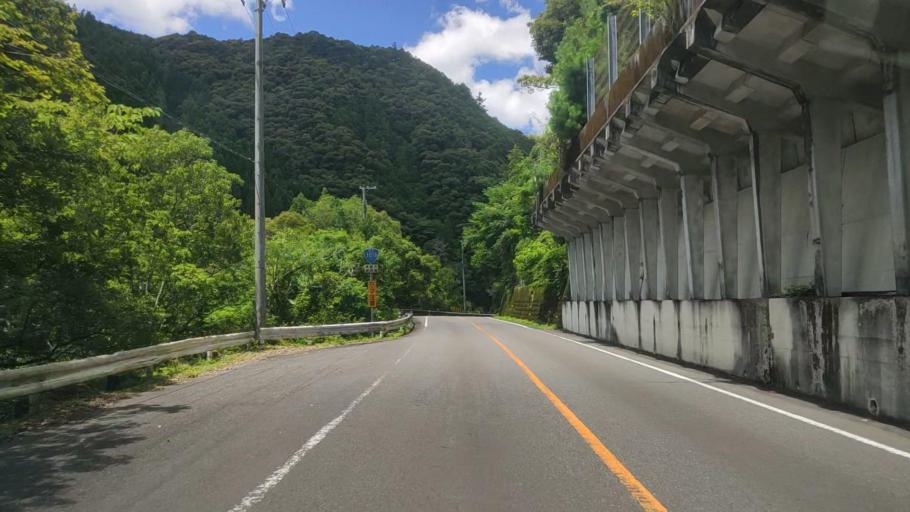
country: JP
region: Mie
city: Owase
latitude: 34.0002
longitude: 136.0096
